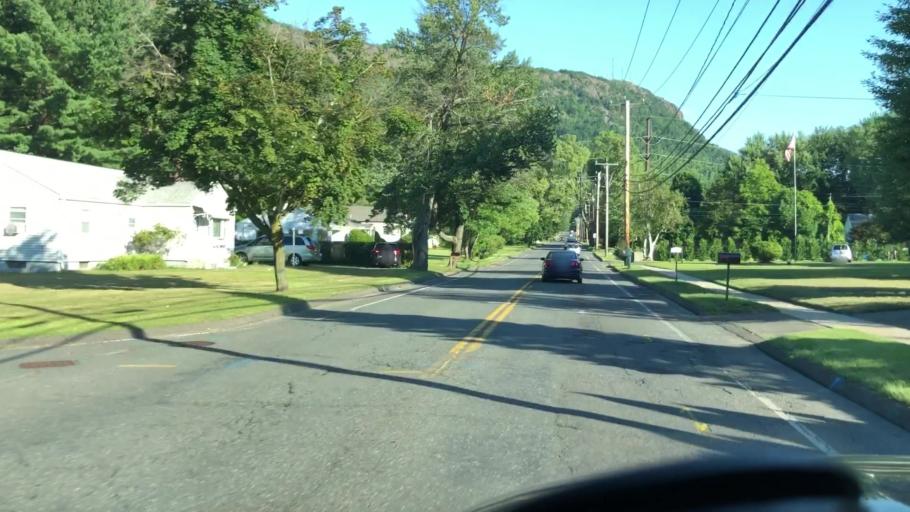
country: US
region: Massachusetts
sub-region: Hampshire County
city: Easthampton
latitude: 42.2548
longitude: -72.6569
